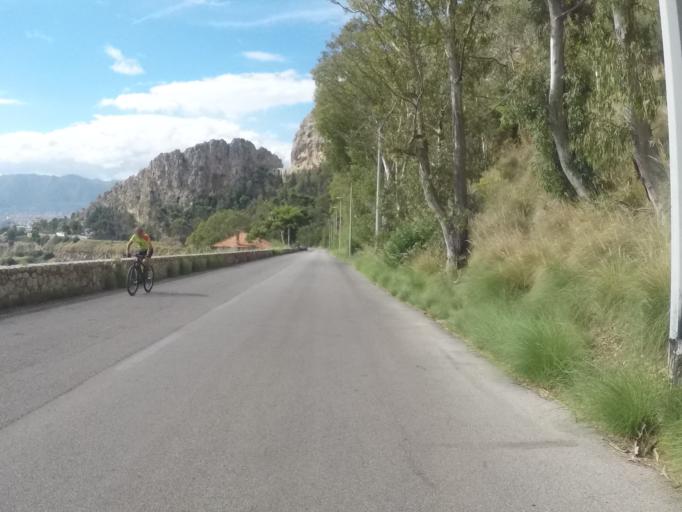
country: IT
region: Sicily
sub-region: Palermo
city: Palermo
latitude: 38.1560
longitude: 13.3672
